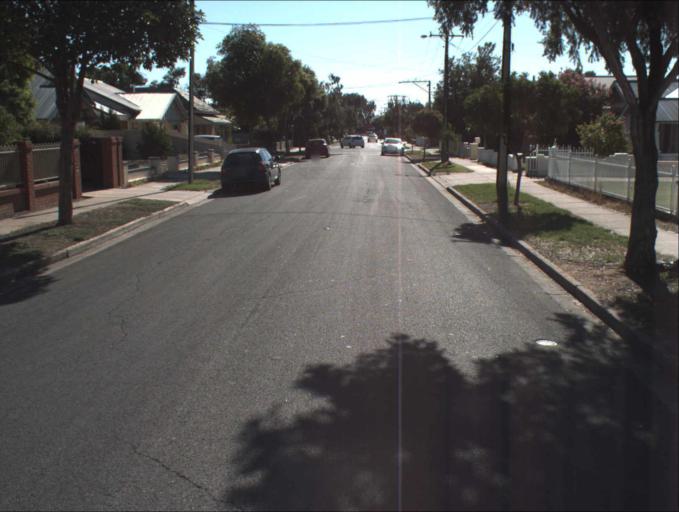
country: AU
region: South Australia
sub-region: Prospect
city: Prospect
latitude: -34.8753
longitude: 138.6059
